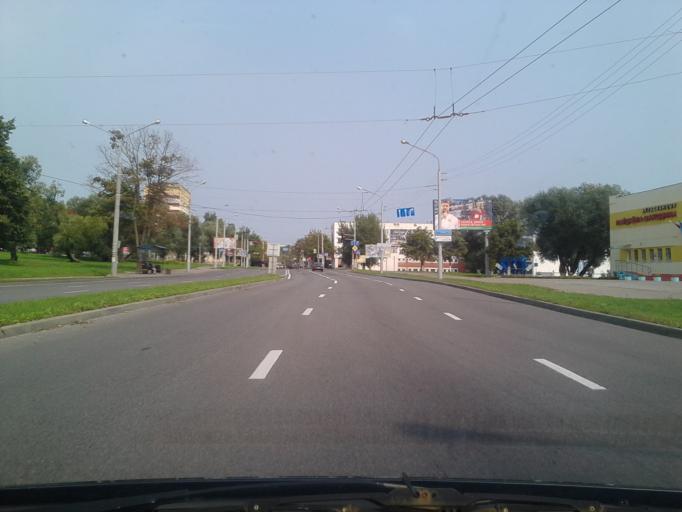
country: BY
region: Minsk
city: Novoye Medvezhino
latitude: 53.8720
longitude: 27.4990
